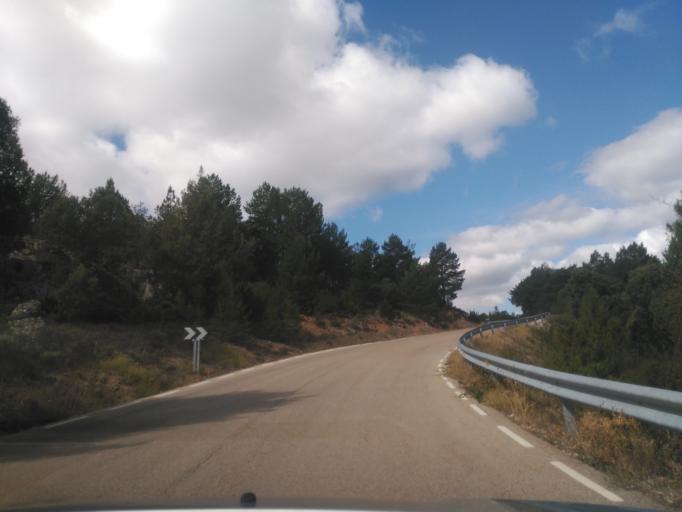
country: ES
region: Castille and Leon
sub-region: Provincia de Soria
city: Espejon
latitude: 41.8407
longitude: -3.2380
